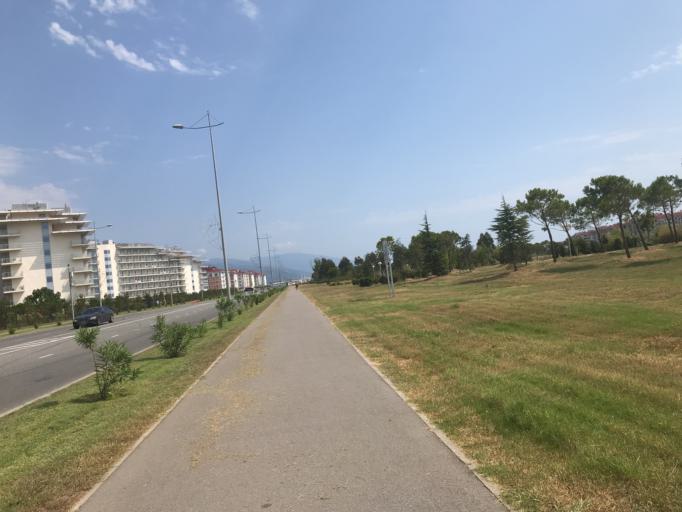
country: RU
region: Krasnodarskiy
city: Adler
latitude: 43.4016
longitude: 39.9724
